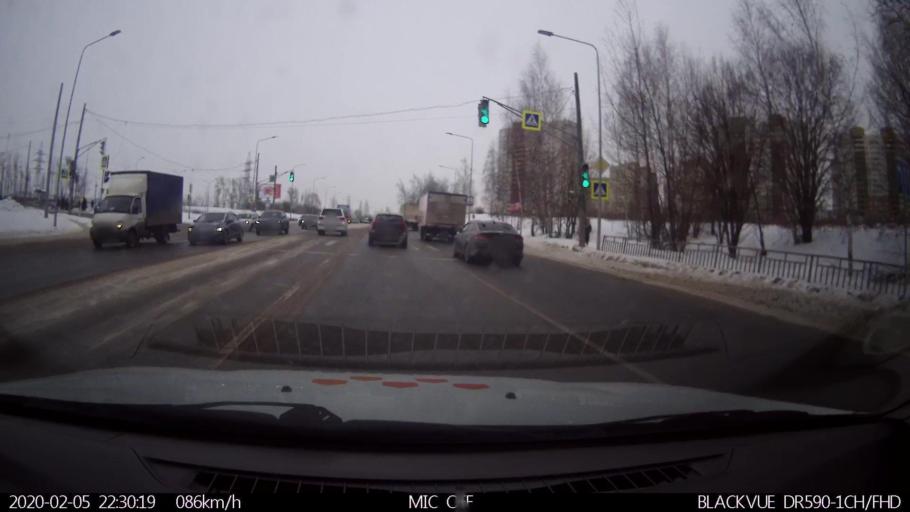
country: RU
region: Nizjnij Novgorod
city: Imeni Stepana Razina
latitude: 54.7437
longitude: 44.1587
